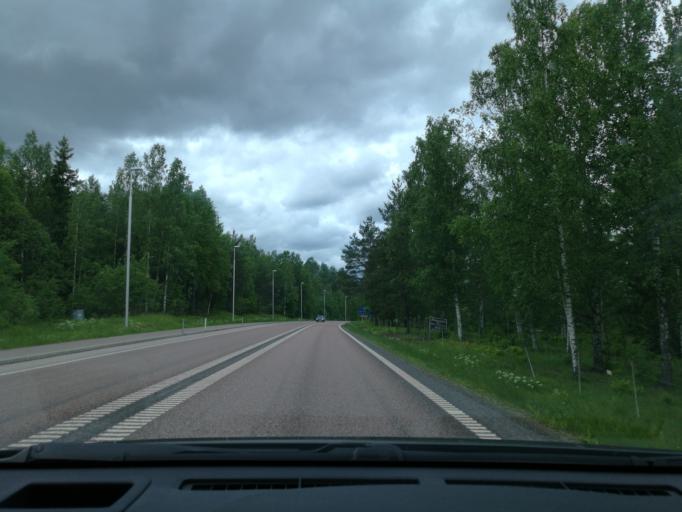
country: SE
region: Vaestmanland
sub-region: Fagersta Kommun
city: Fagersta
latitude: 59.9789
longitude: 15.8193
